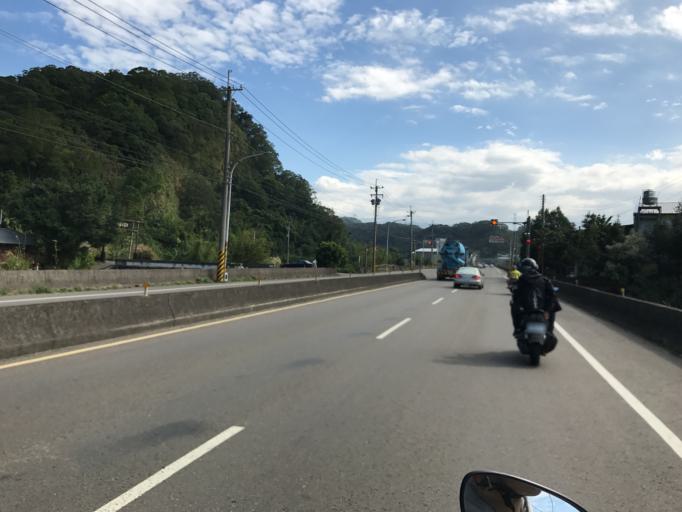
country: TW
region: Taiwan
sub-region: Hsinchu
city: Zhubei
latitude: 24.7376
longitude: 121.1136
